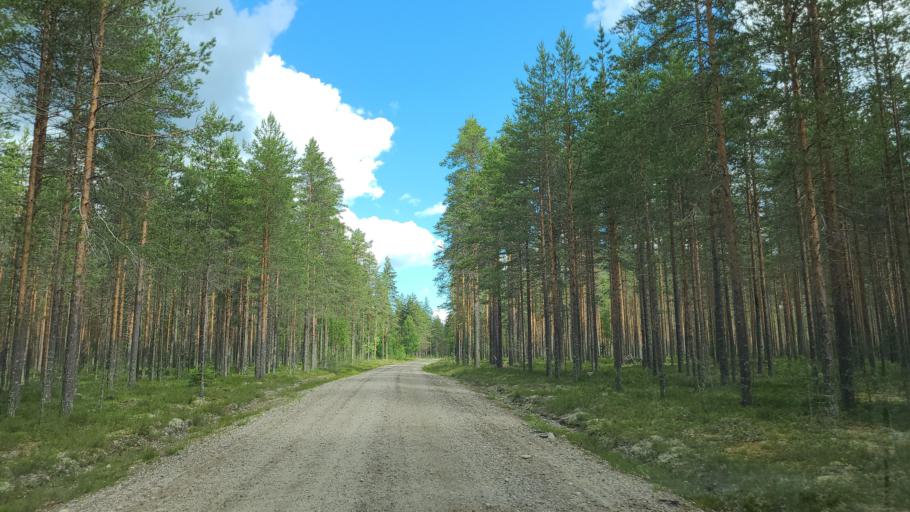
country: FI
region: Northern Savo
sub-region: Koillis-Savo
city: Kaavi
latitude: 63.0562
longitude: 28.8238
